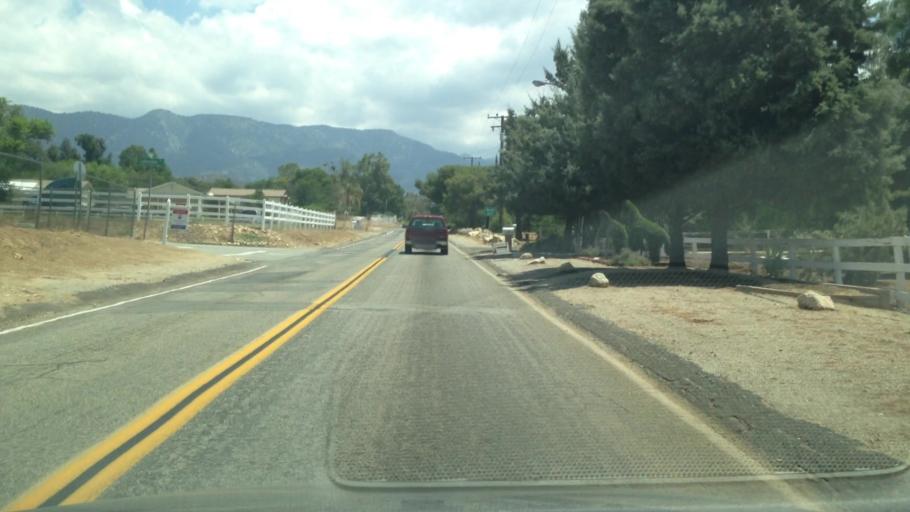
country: US
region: California
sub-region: Riverside County
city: Cherry Valley
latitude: 33.9823
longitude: -116.9734
